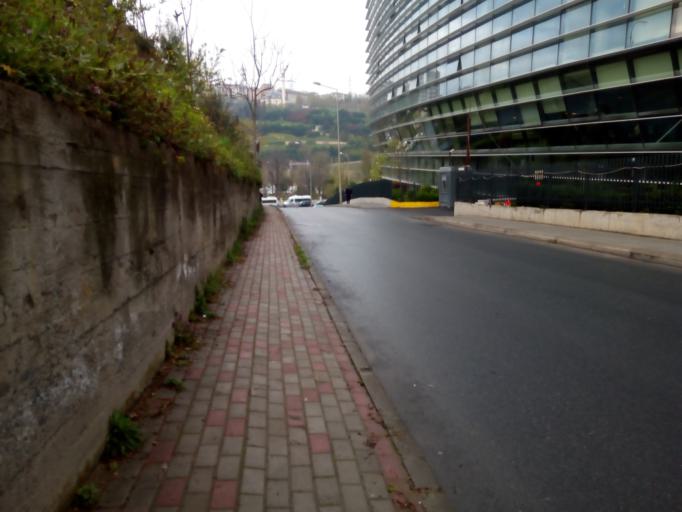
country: TR
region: Istanbul
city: Sisli
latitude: 41.0709
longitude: 28.9668
